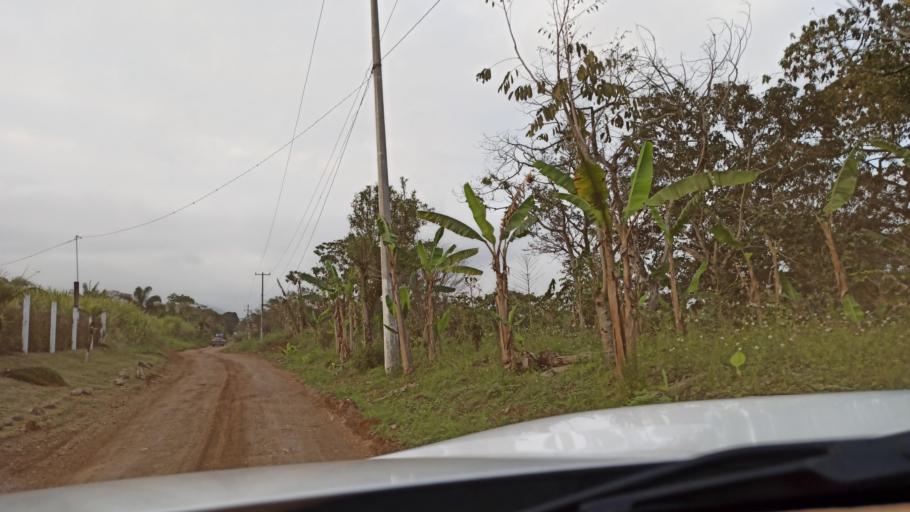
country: MX
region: Veracruz
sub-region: Fortin
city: Fortin de las Flores
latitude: 18.9215
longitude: -97.0046
